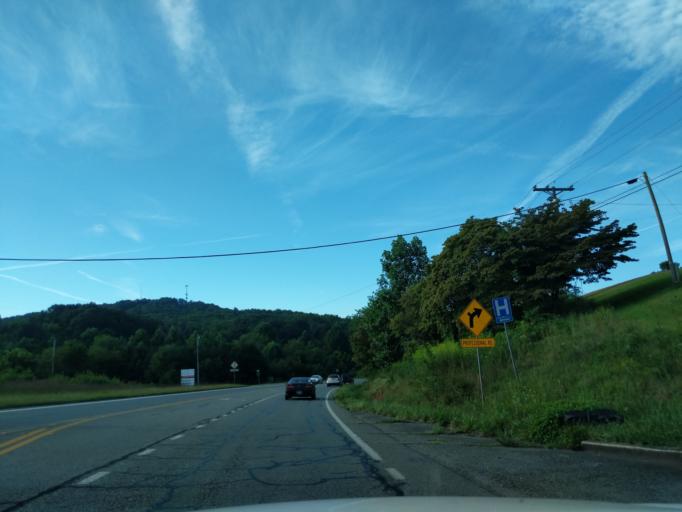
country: US
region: Georgia
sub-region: Fannin County
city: McCaysville
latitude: 34.9154
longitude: -84.3762
